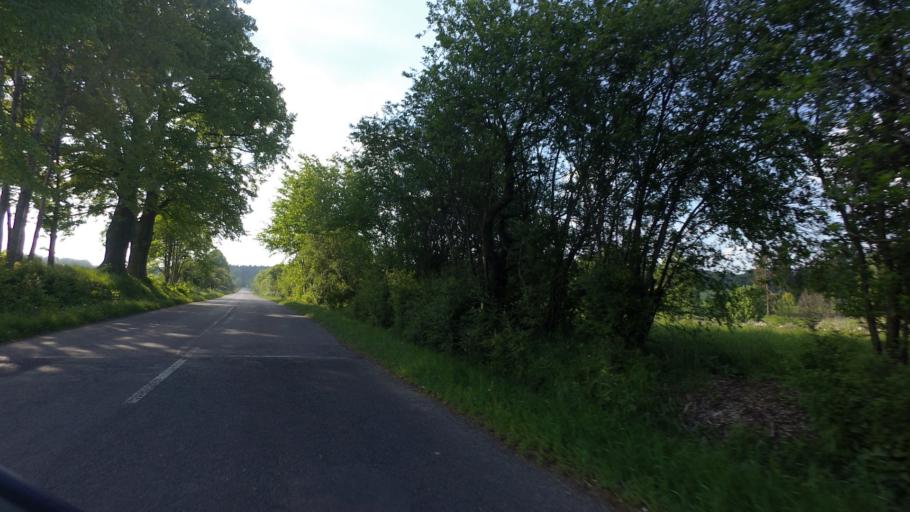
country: CZ
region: Ustecky
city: Vilemov
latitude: 51.0133
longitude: 14.3506
